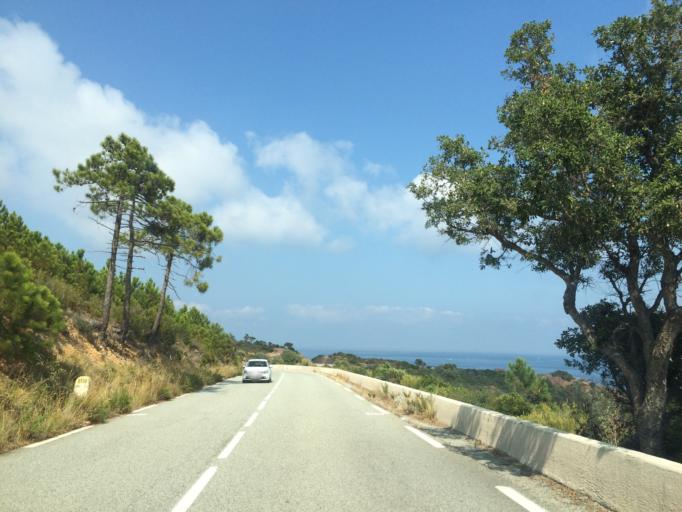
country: FR
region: Provence-Alpes-Cote d'Azur
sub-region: Departement des Alpes-Maritimes
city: Theoule-sur-Mer
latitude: 43.4483
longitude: 6.9133
